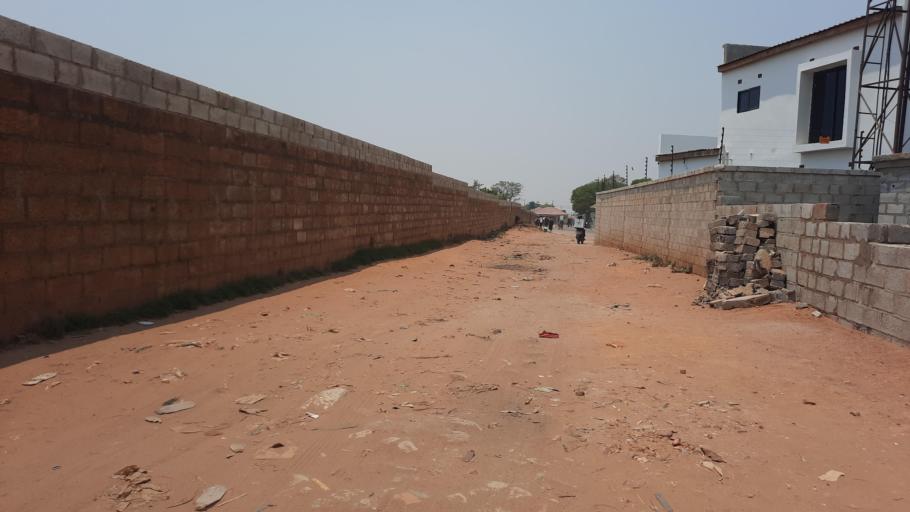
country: ZM
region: Lusaka
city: Lusaka
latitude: -15.4091
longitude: 28.3672
